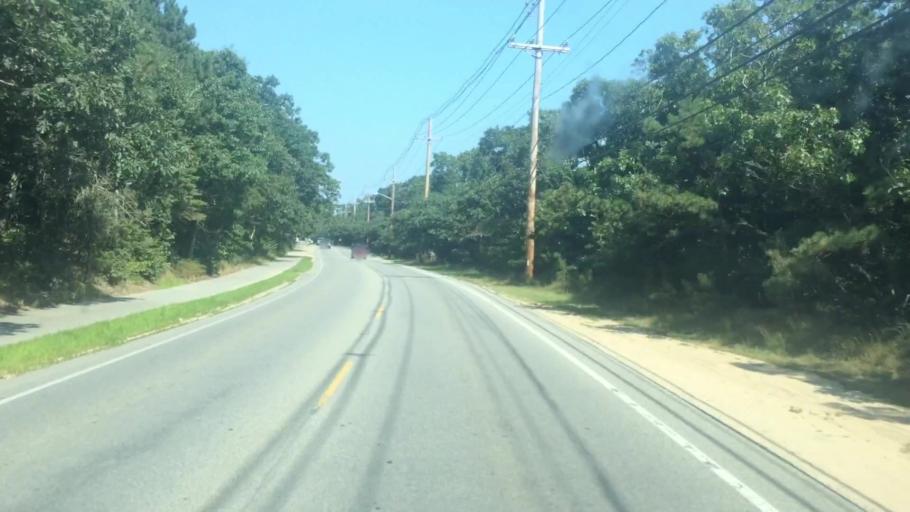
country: US
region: Massachusetts
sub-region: Dukes County
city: Vineyard Haven
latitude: 41.4352
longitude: -70.6079
